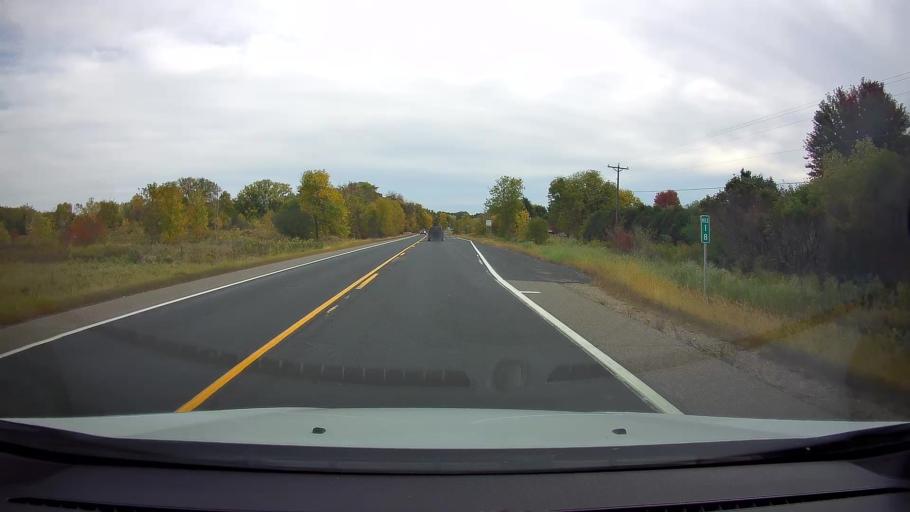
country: US
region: Minnesota
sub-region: Washington County
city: Stillwater
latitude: 45.0795
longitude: -92.8377
